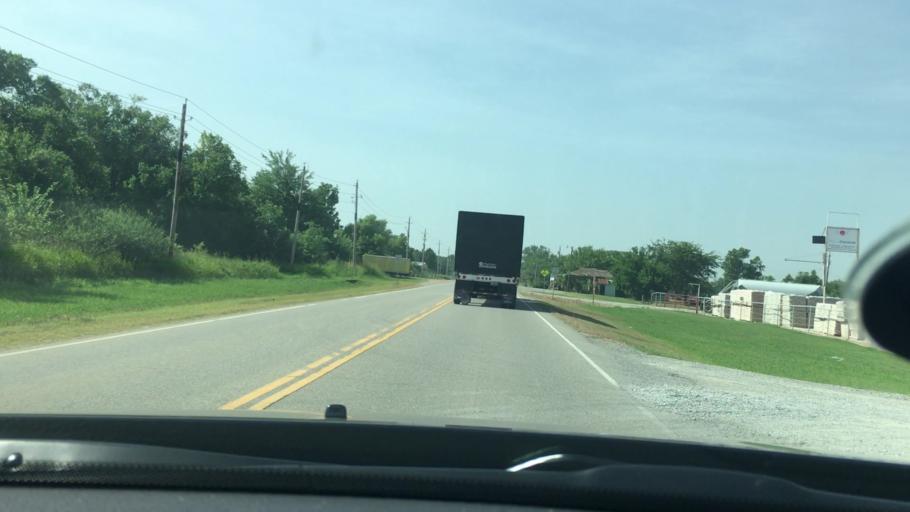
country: US
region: Oklahoma
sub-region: Coal County
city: Coalgate
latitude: 34.4729
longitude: -96.2177
